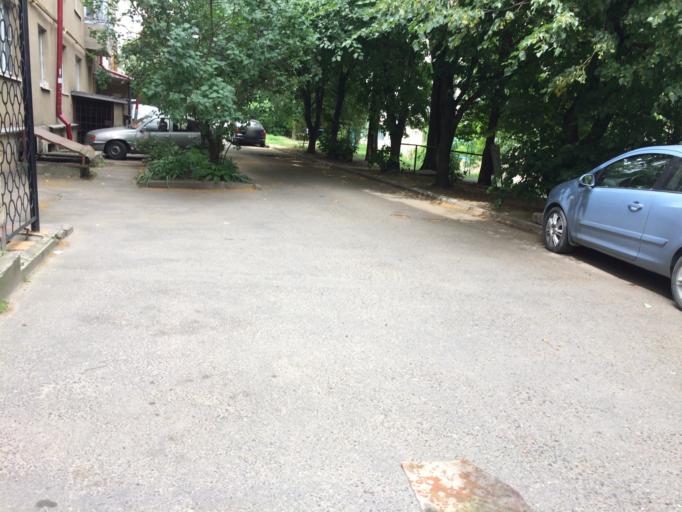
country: RU
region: Stavropol'skiy
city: Stavropol'
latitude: 45.0409
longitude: 41.9552
